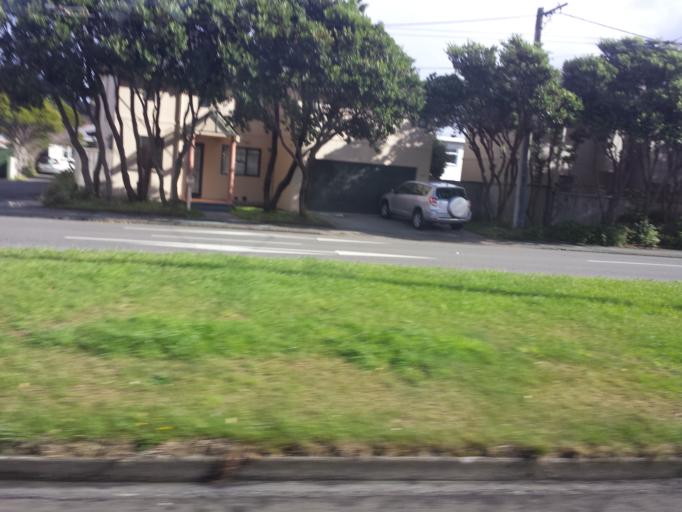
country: NZ
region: Wellington
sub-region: Wellington City
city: Wellington
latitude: -41.3187
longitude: 174.8024
